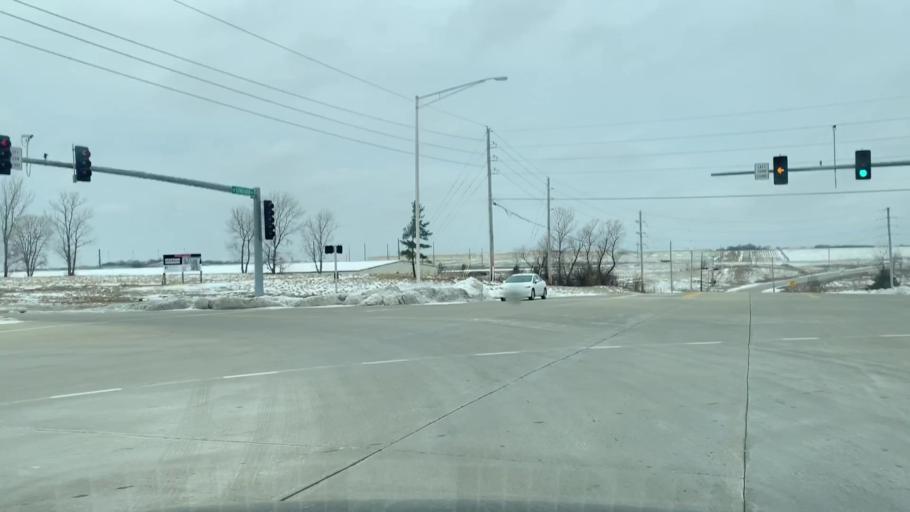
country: US
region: Missouri
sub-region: Jackson County
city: Lees Summit
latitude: 38.9681
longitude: -94.3618
